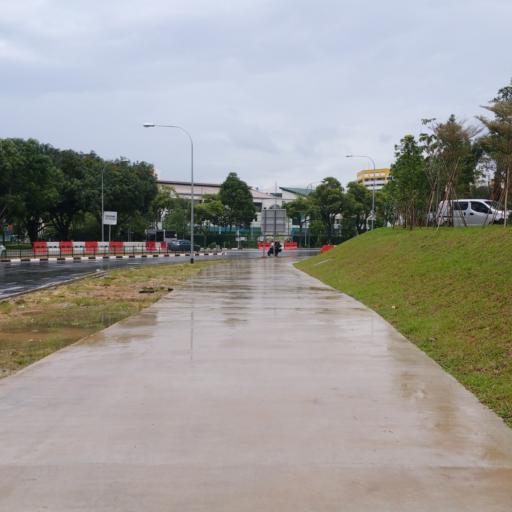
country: MY
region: Johor
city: Kampung Pasir Gudang Baru
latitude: 1.4135
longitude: 103.8391
